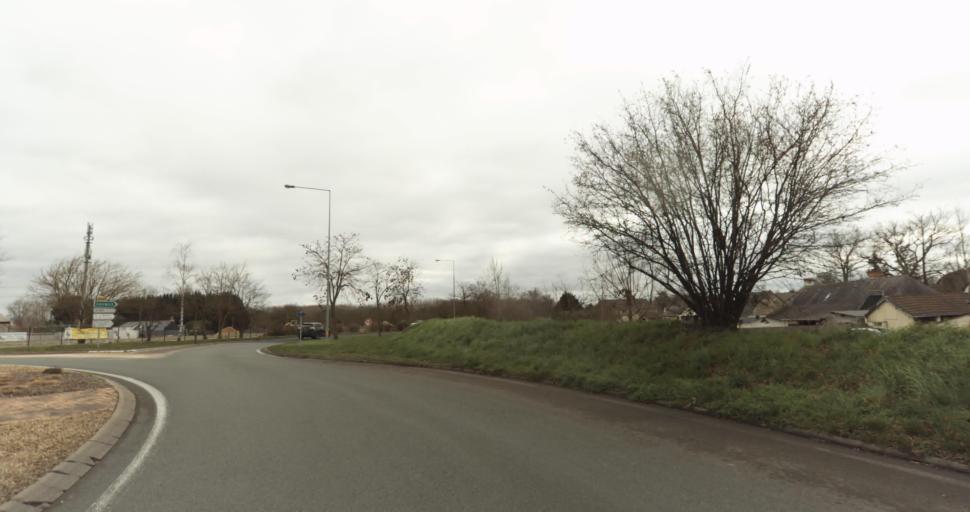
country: FR
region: Pays de la Loire
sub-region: Departement de Maine-et-Loire
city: Jumelles
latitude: 47.3886
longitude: -0.1165
